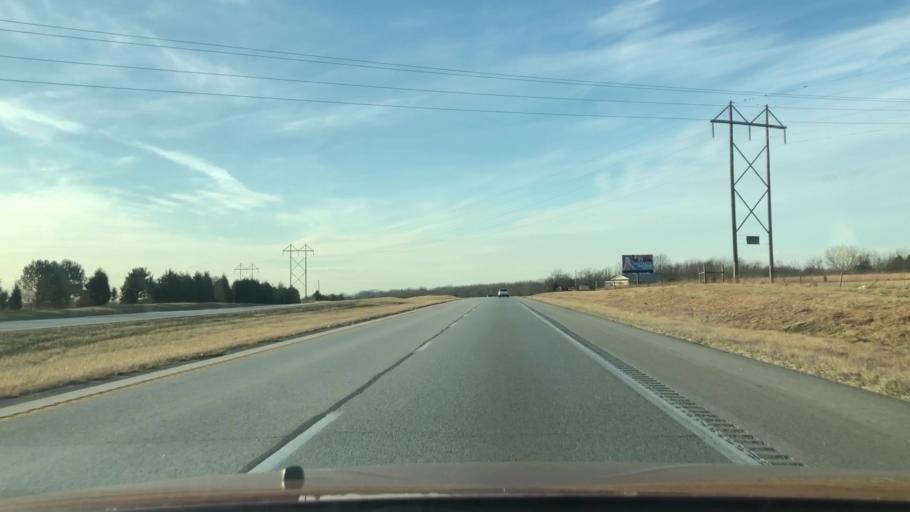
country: US
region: Missouri
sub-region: Webster County
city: Seymour
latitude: 37.1165
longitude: -92.6775
